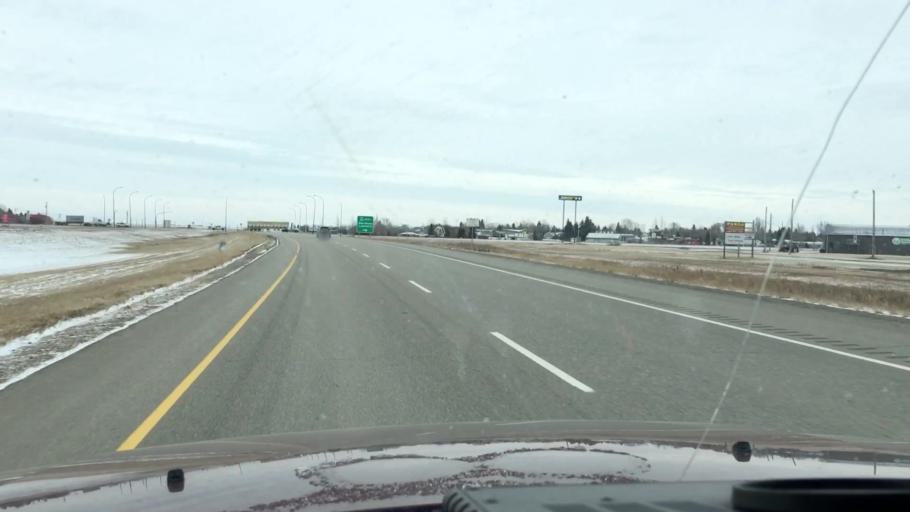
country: CA
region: Saskatchewan
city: Watrous
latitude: 51.2716
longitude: -105.9994
